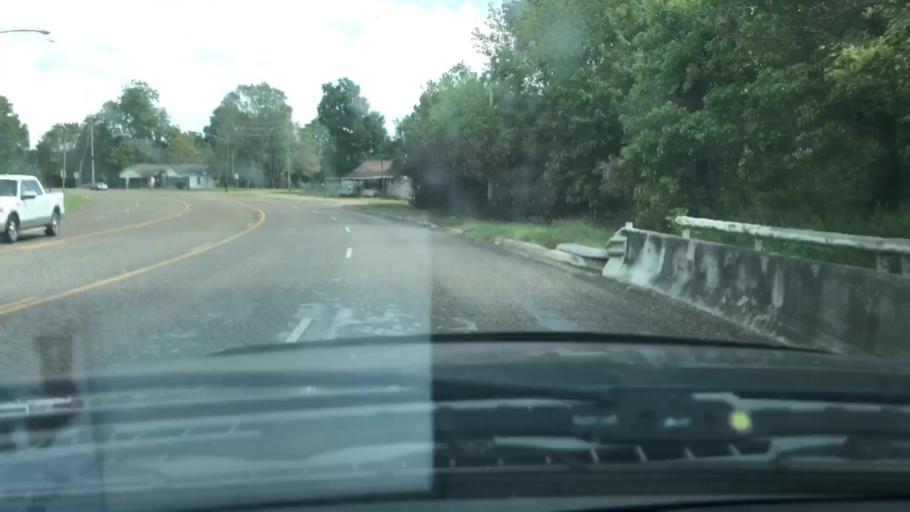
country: US
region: Texas
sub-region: Bowie County
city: Texarkana
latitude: 33.4053
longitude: -94.0615
